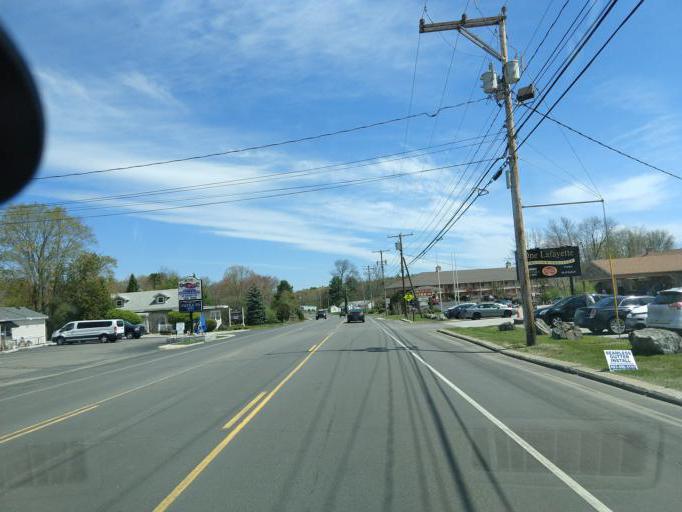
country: US
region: New Hampshire
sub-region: Rockingham County
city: Seabrook
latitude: 42.9036
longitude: -70.8673
